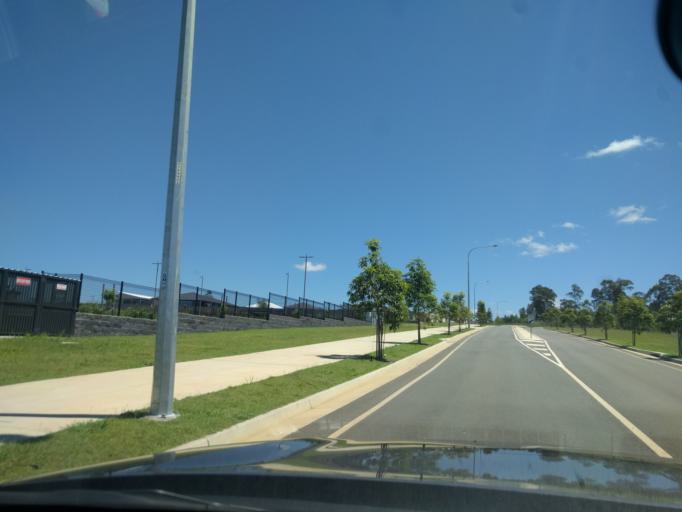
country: AU
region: Queensland
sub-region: Logan
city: Cedar Vale
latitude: -27.9900
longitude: 153.0126
